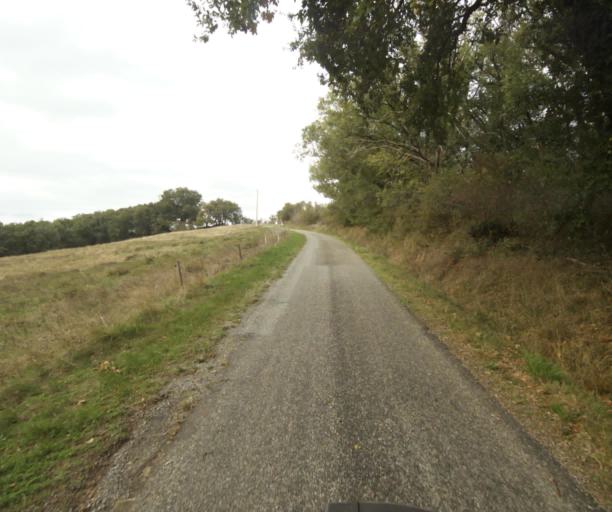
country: FR
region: Midi-Pyrenees
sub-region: Departement du Tarn-et-Garonne
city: Beaumont-de-Lomagne
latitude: 43.8295
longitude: 1.0760
